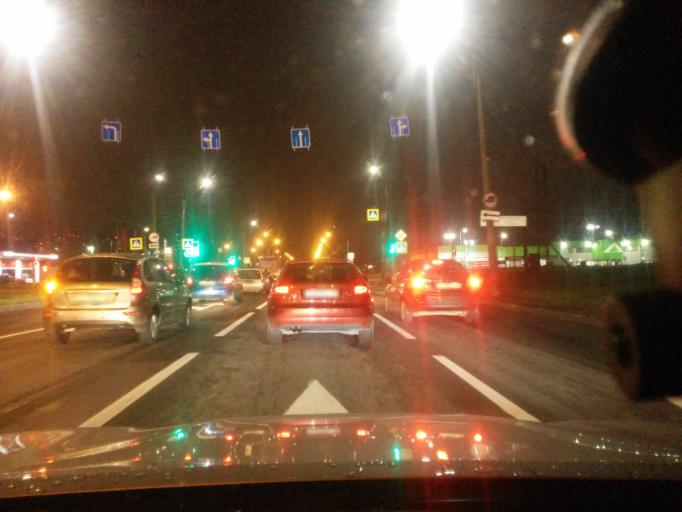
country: RU
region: Leningrad
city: Parnas
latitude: 60.0651
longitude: 30.3445
